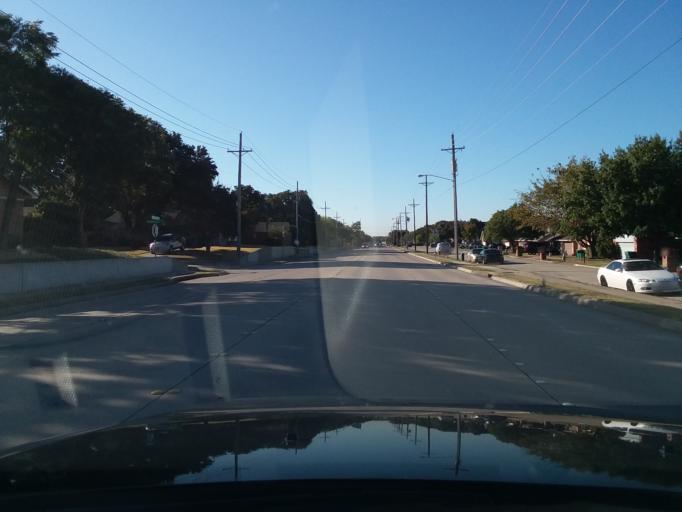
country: US
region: Texas
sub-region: Denton County
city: Lewisville
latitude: 33.0335
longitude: -97.0276
